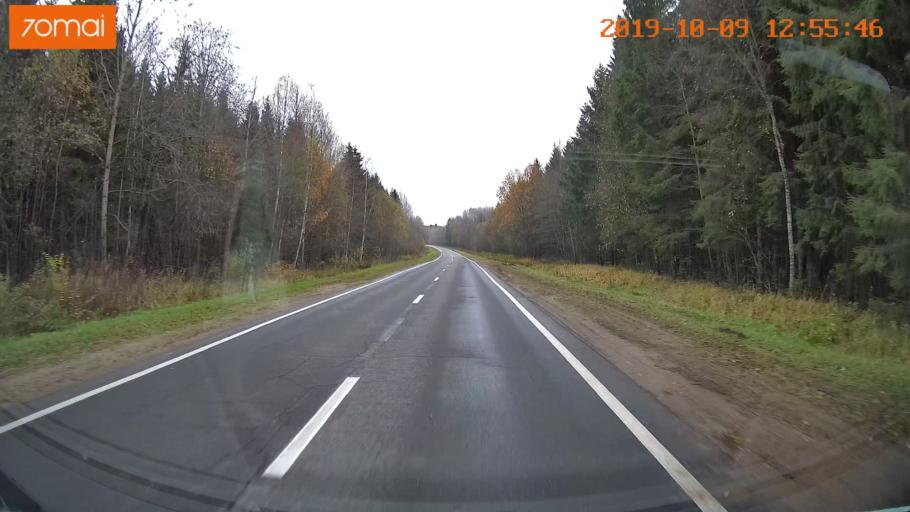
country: RU
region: Jaroslavl
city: Prechistoye
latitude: 58.3977
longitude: 40.4015
